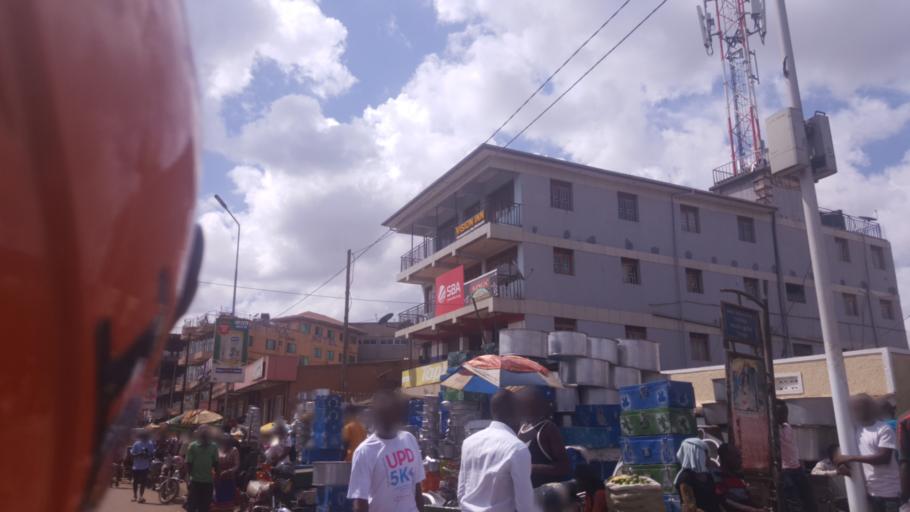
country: UG
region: Central Region
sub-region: Kampala District
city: Kampala
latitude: 0.3094
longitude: 32.5732
